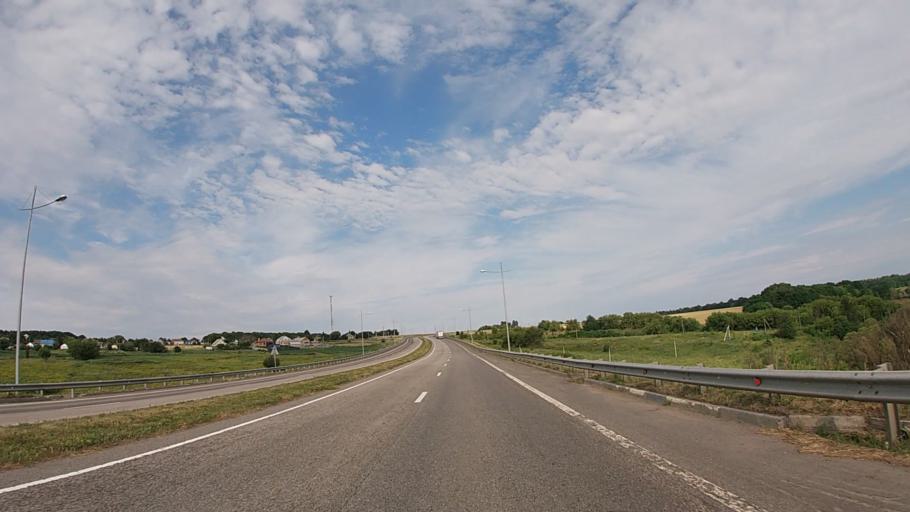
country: RU
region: Belgorod
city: Tomarovka
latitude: 50.7069
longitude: 36.2041
